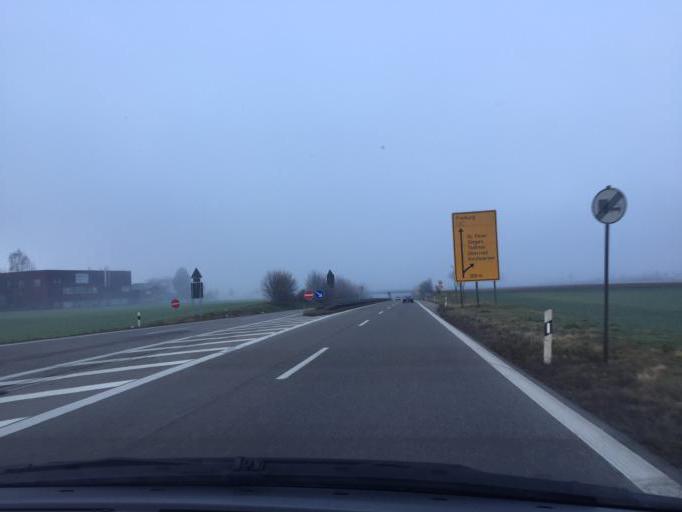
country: DE
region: Baden-Wuerttemberg
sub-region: Freiburg Region
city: Kirchzarten
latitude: 47.9725
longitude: 7.9572
